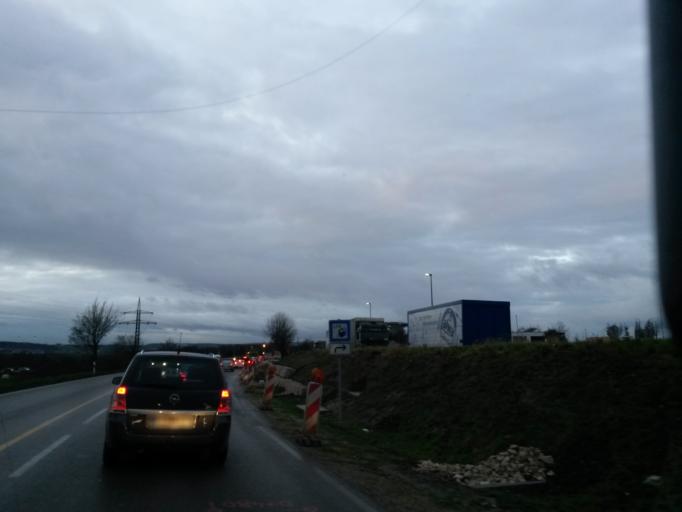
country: DE
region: Baden-Wuerttemberg
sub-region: Regierungsbezirk Stuttgart
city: Denkendorf
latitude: 48.7069
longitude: 9.3083
